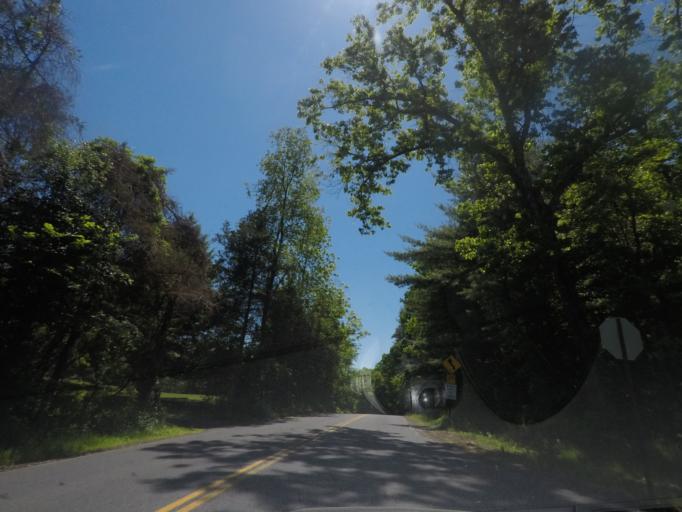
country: US
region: New York
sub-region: Saratoga County
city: Mechanicville
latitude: 42.9447
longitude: -73.7086
